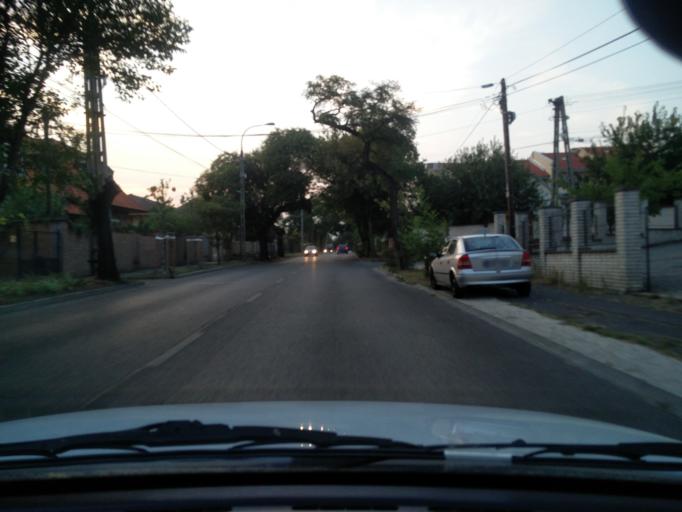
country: HU
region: Budapest
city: Budapest XXI. keruelet
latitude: 47.4119
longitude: 19.0875
